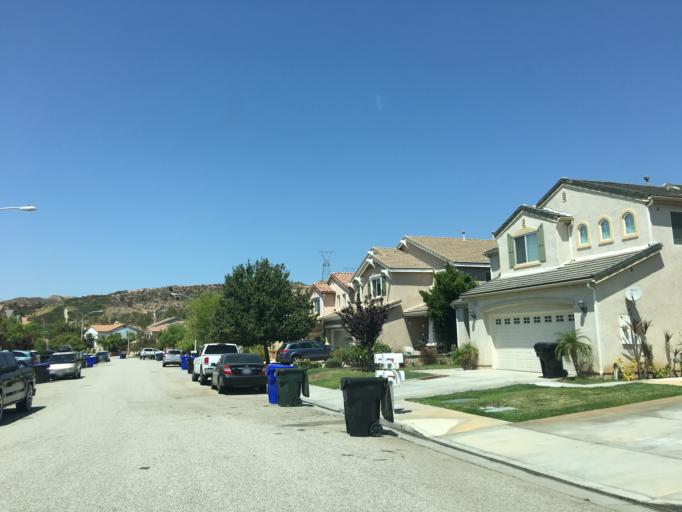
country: US
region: California
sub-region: Los Angeles County
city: Valencia
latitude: 34.4654
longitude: -118.5592
